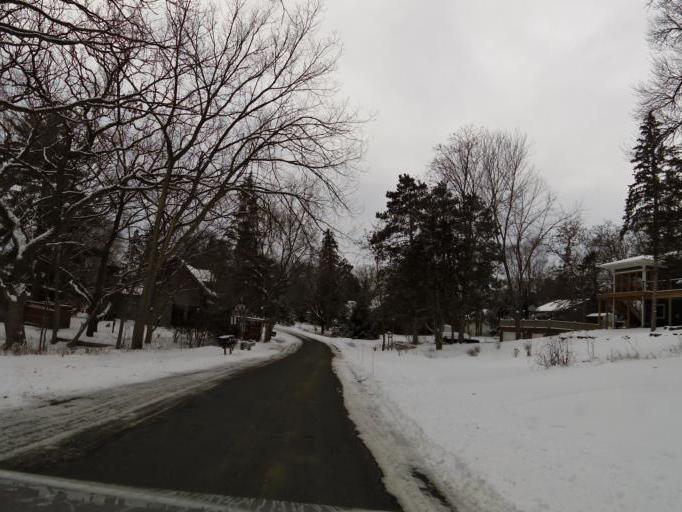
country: US
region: Minnesota
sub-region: Washington County
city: Lake Saint Croix Beach
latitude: 44.9274
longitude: -92.7658
